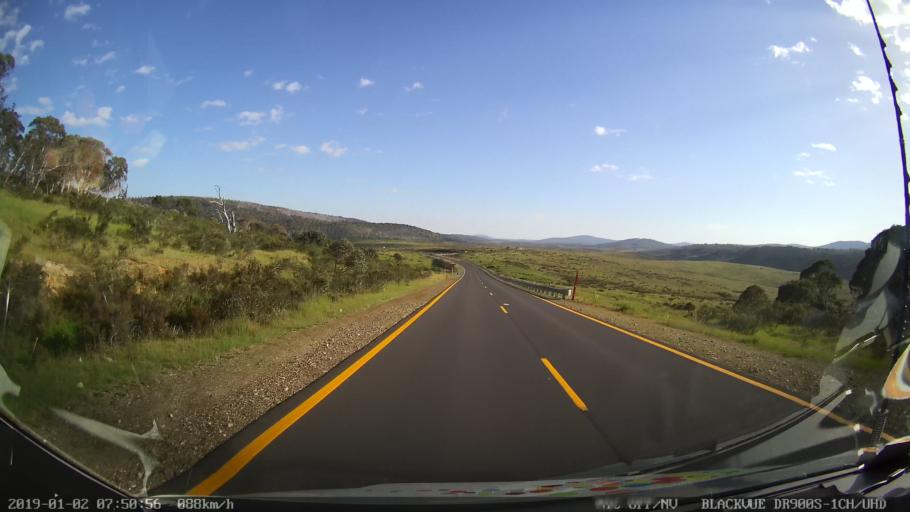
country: AU
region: New South Wales
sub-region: Tumut Shire
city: Tumut
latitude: -35.7245
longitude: 148.5299
